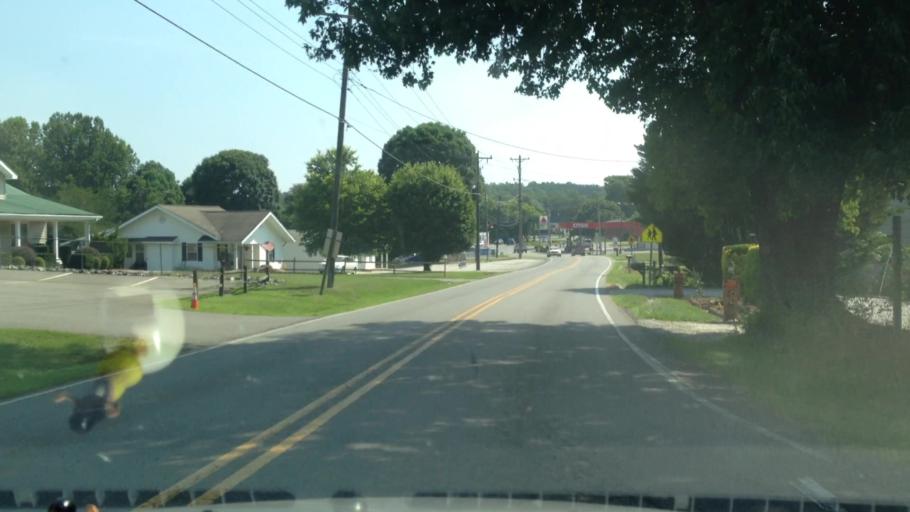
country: US
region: North Carolina
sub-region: Surry County
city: Flat Rock
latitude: 36.5109
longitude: -80.5722
